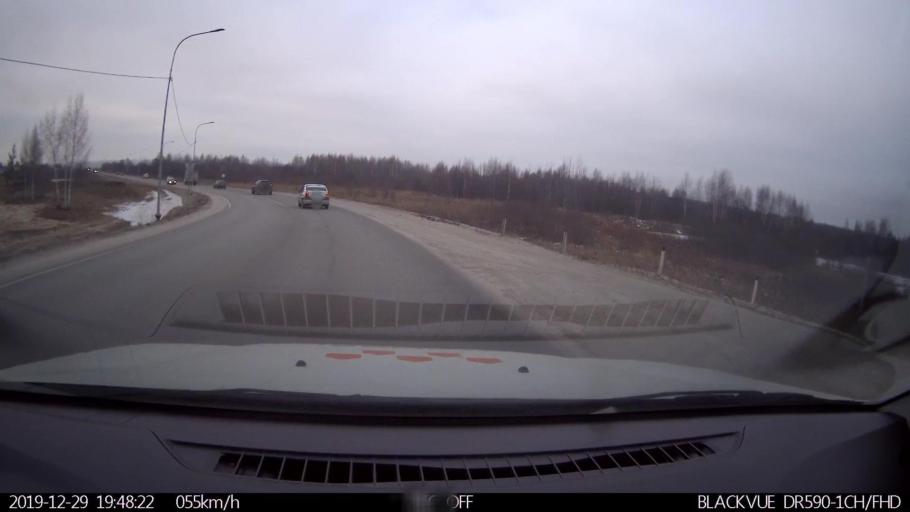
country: RU
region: Nizjnij Novgorod
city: Neklyudovo
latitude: 56.3846
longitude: 44.0096
